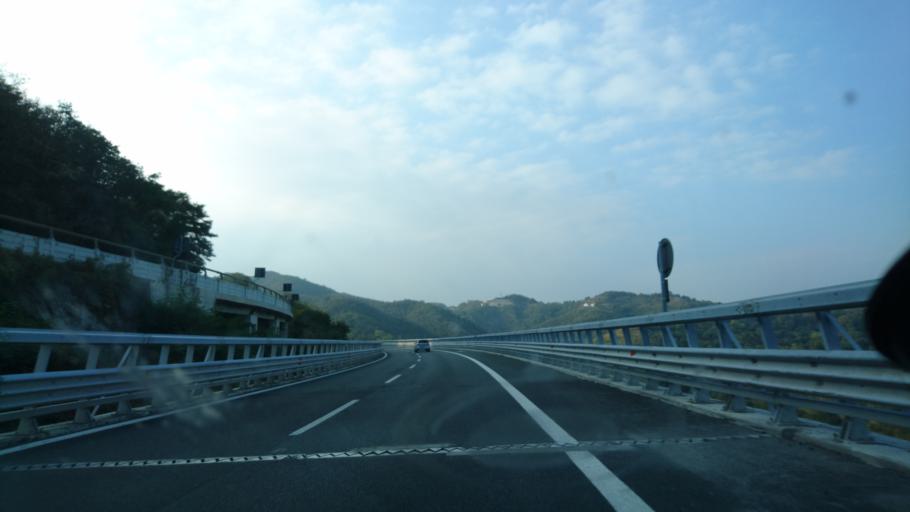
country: IT
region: Liguria
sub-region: Provincia di Savona
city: Altare
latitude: 44.3232
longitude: 8.3760
